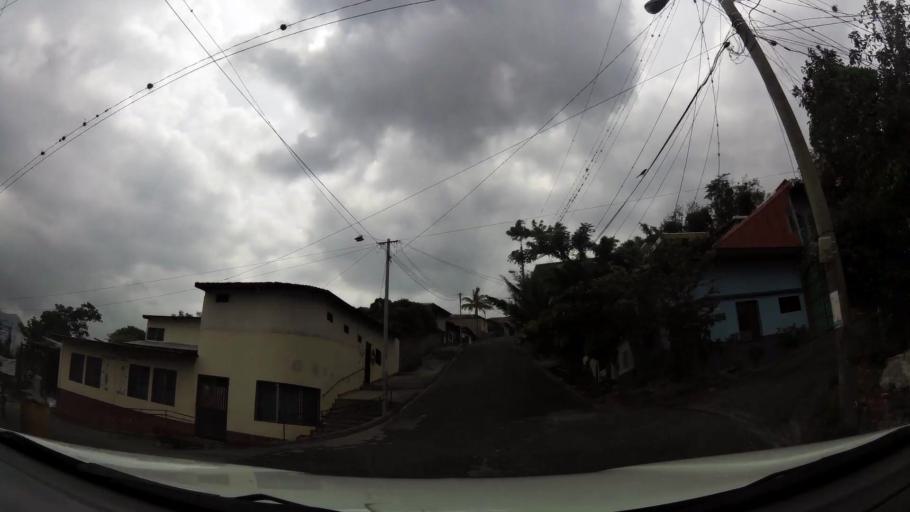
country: NI
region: Matagalpa
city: Matagalpa
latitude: 12.9224
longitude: -85.9160
